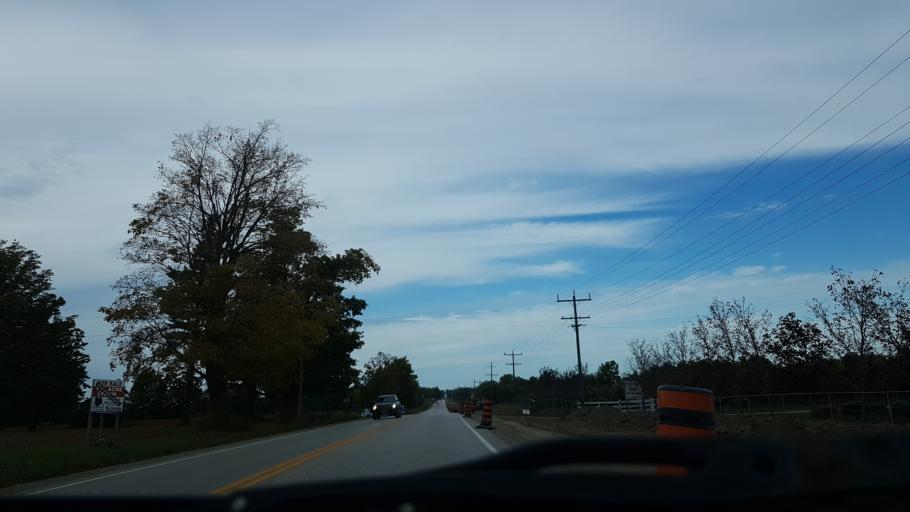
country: CA
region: Ontario
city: Wasaga Beach
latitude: 44.3808
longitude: -80.0878
